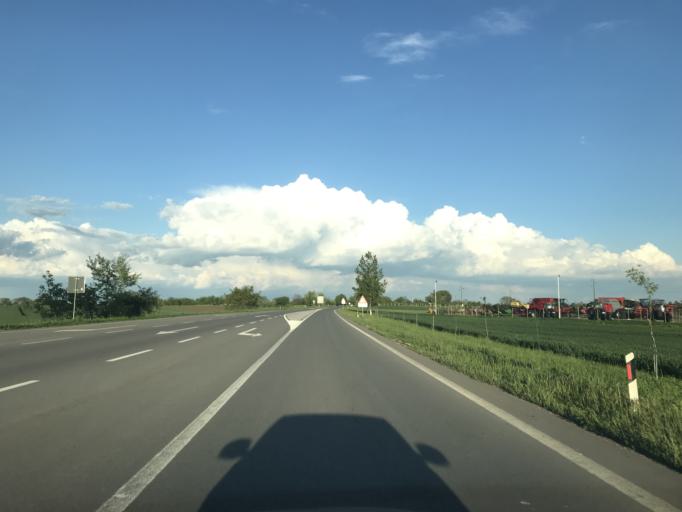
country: RS
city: Aradac
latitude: 45.3919
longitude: 20.2979
